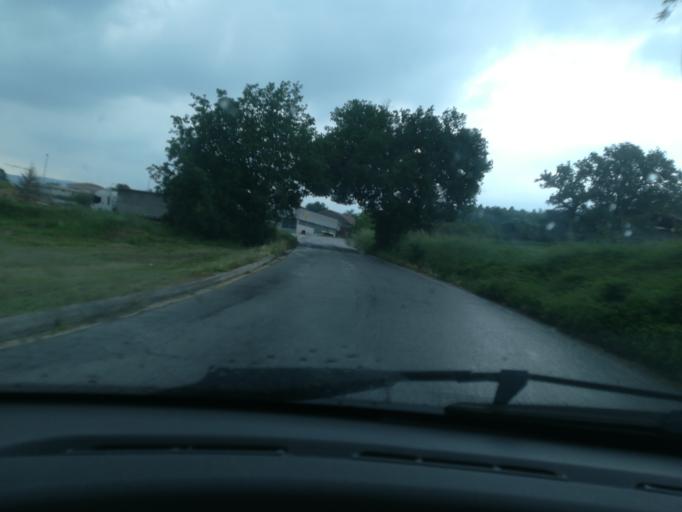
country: IT
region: The Marches
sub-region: Provincia di Macerata
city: Treia
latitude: 43.3035
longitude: 13.3135
